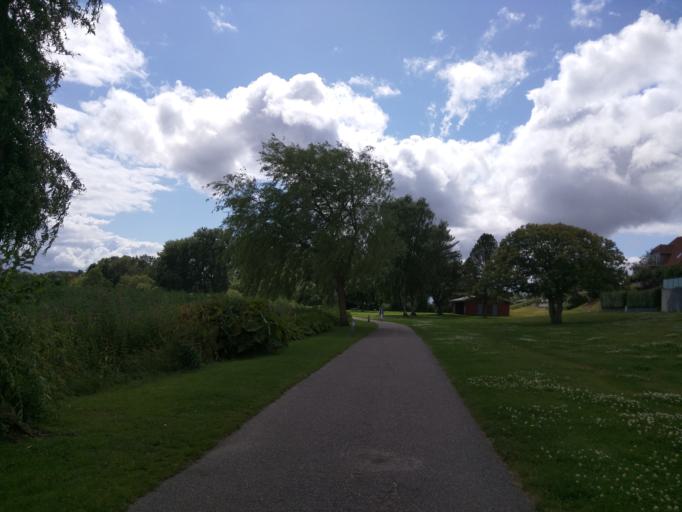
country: DK
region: Central Jutland
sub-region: Viborg Kommune
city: Viborg
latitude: 56.4408
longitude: 9.4044
